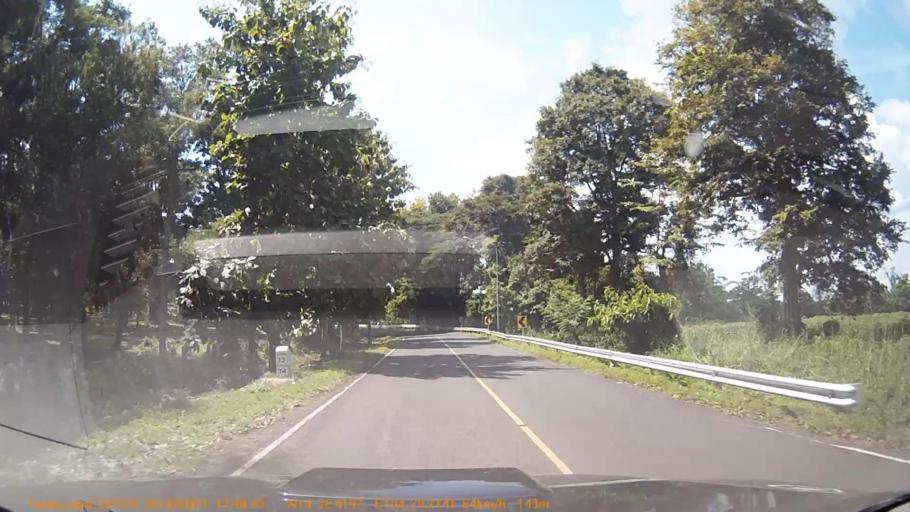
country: TH
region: Sisaket
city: Khun Han
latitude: 14.5406
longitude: 104.4866
